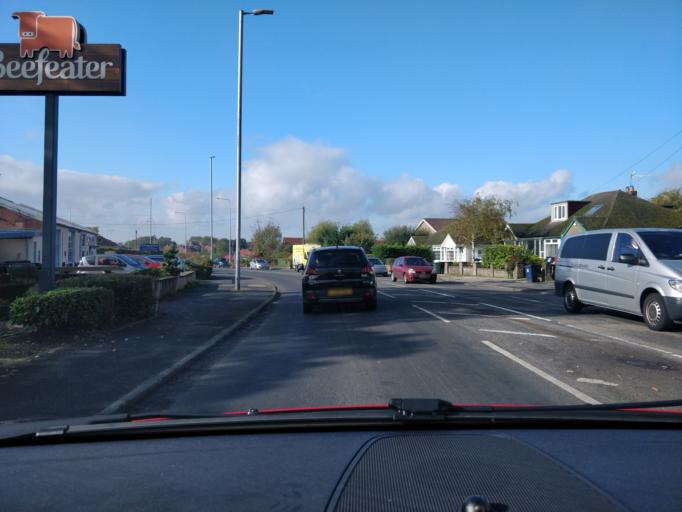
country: GB
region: England
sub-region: Lancashire
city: Ormskirk
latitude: 53.6105
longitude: -2.9346
